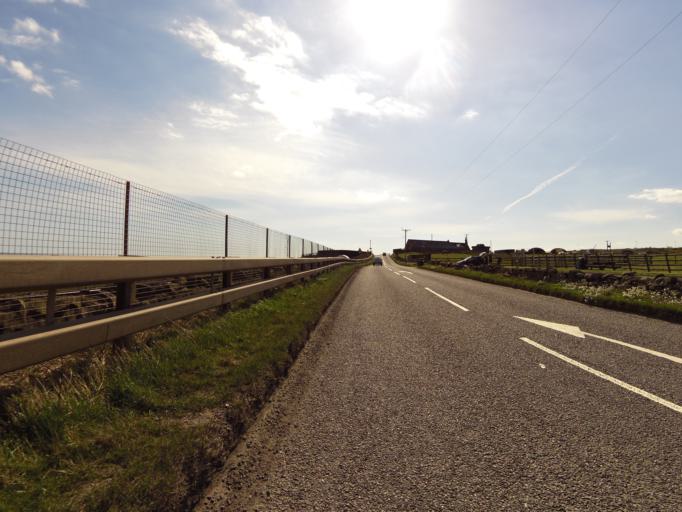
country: GB
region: Scotland
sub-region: Aberdeen City
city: Aberdeen
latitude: 57.1229
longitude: -2.0566
